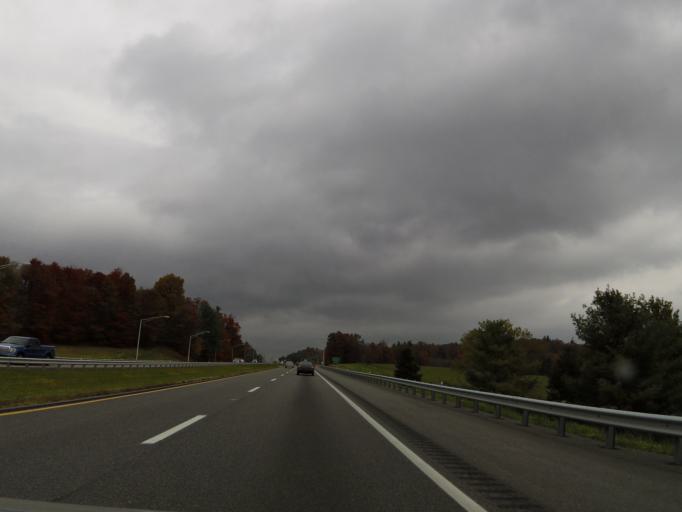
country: US
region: Virginia
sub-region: Bland County
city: Bland
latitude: 37.0798
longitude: -81.1263
